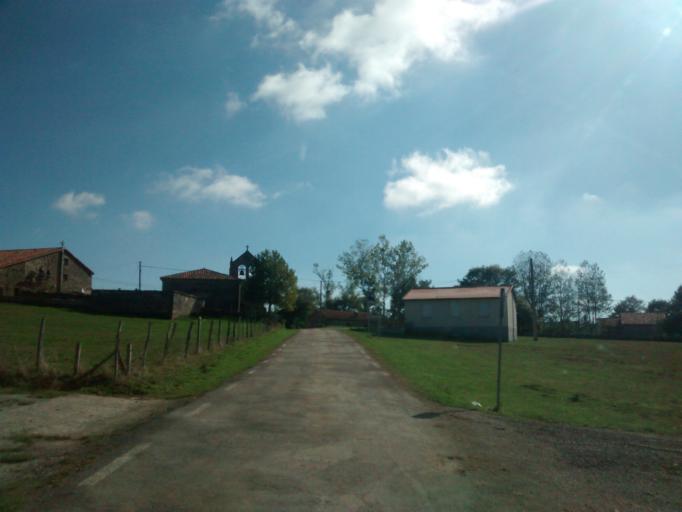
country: ES
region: Castille and Leon
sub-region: Provincia de Burgos
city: Arija
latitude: 42.9271
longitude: -4.0015
